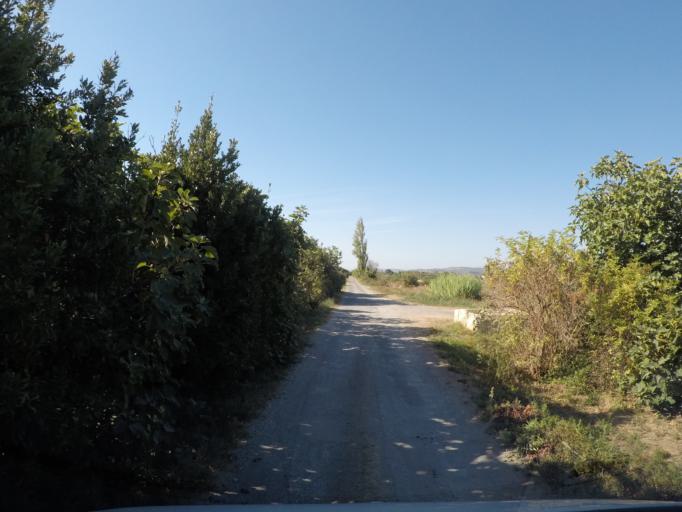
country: FR
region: Languedoc-Roussillon
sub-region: Departement de l'Aude
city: Narbonne
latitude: 43.1760
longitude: 3.0183
